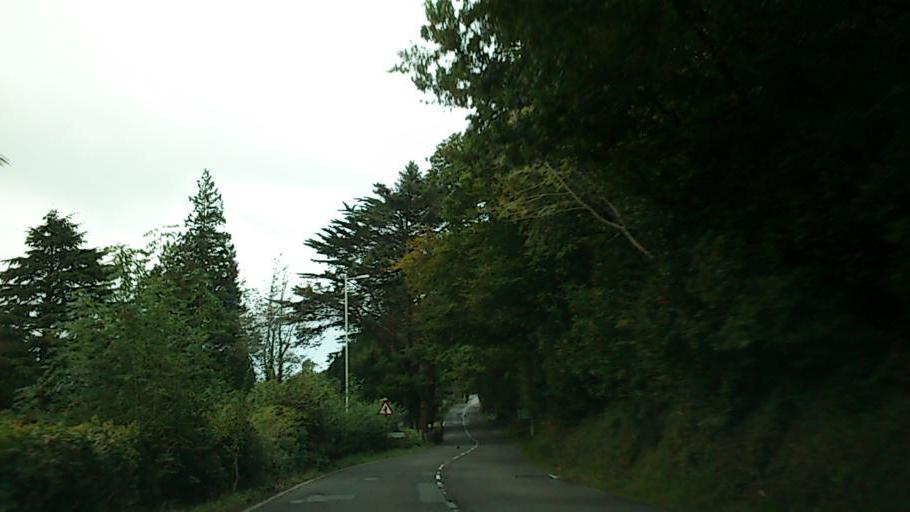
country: GB
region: Wales
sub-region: Sir Powys
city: Machynlleth
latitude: 52.5404
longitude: -3.9394
